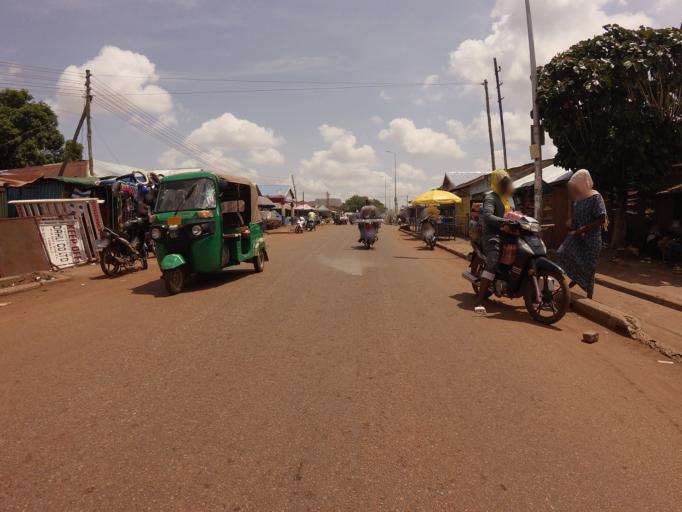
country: GH
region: Northern
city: Tamale
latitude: 9.4014
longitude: -0.8445
